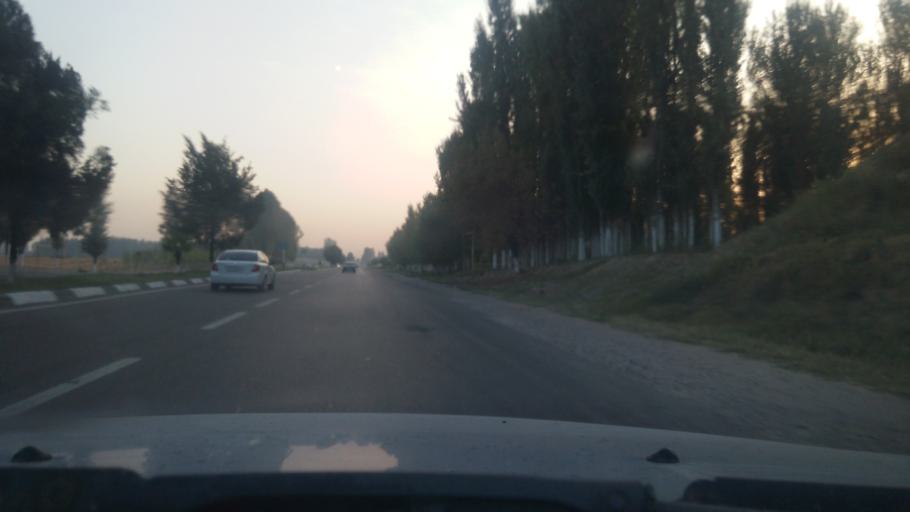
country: UZ
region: Toshkent
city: Amir Timur
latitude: 41.0698
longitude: 68.9230
